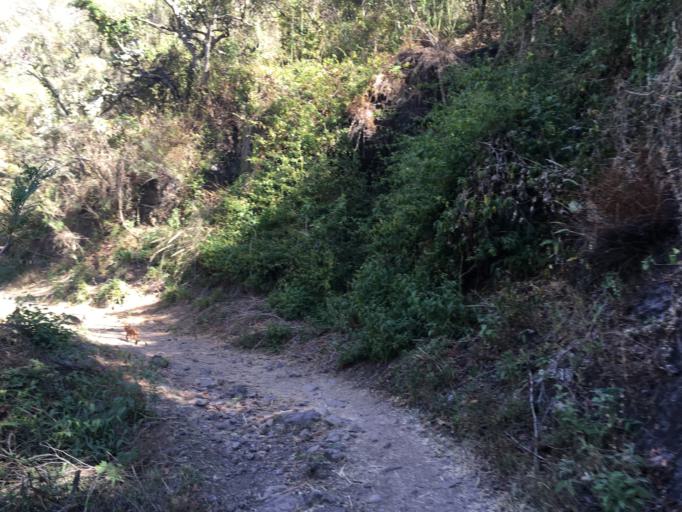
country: MX
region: Michoacan
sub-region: Morelia
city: Montana Monarca (Punta Altozano)
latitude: 19.6766
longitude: -101.1522
